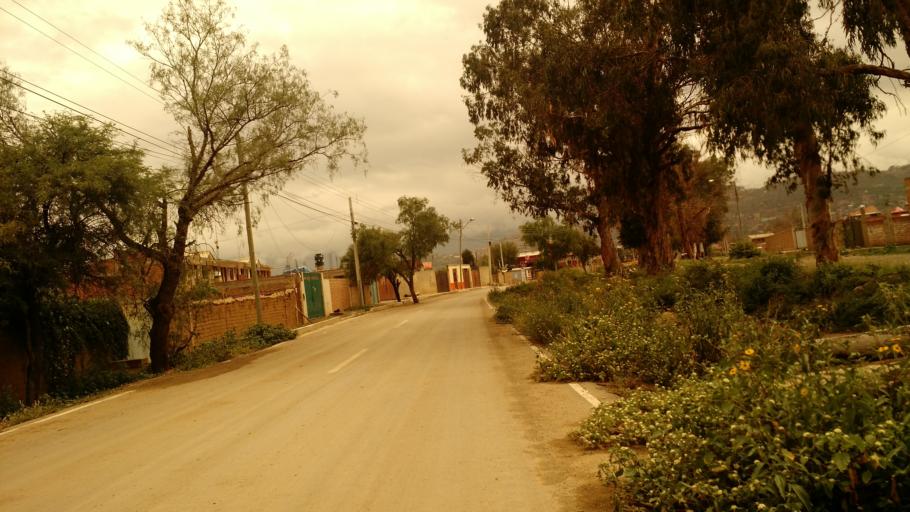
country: BO
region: Cochabamba
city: Cochabamba
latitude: -17.4521
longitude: -66.1540
